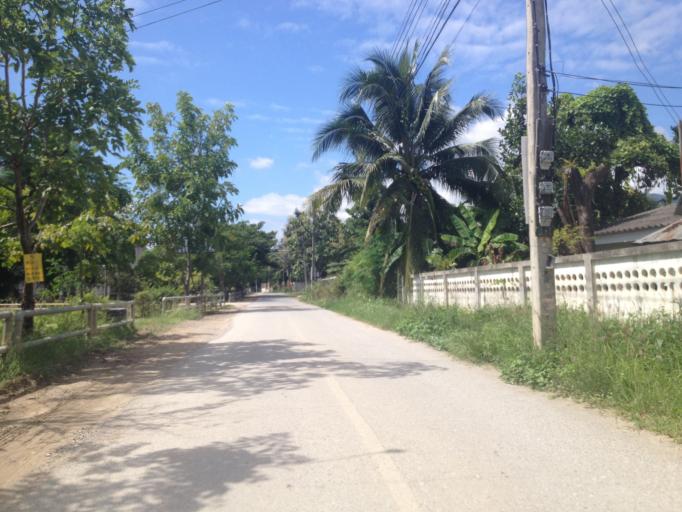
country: TH
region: Chiang Mai
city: Chiang Mai
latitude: 18.7613
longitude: 98.9523
